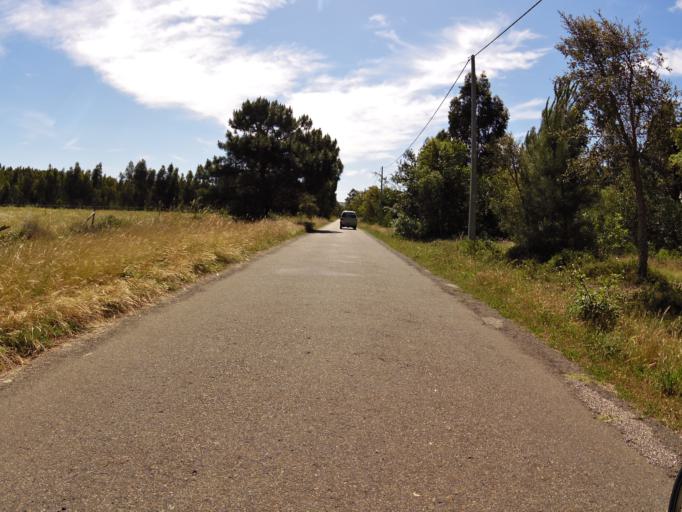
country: PT
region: Setubal
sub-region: Sines
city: Porto Covo
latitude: 37.9372
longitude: -8.7675
